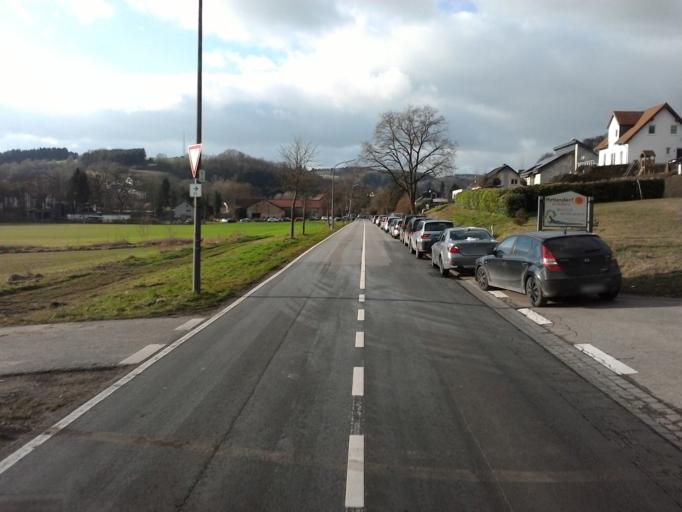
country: DE
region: Rheinland-Pfalz
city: Mettendorf
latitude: 49.9418
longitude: 6.3406
